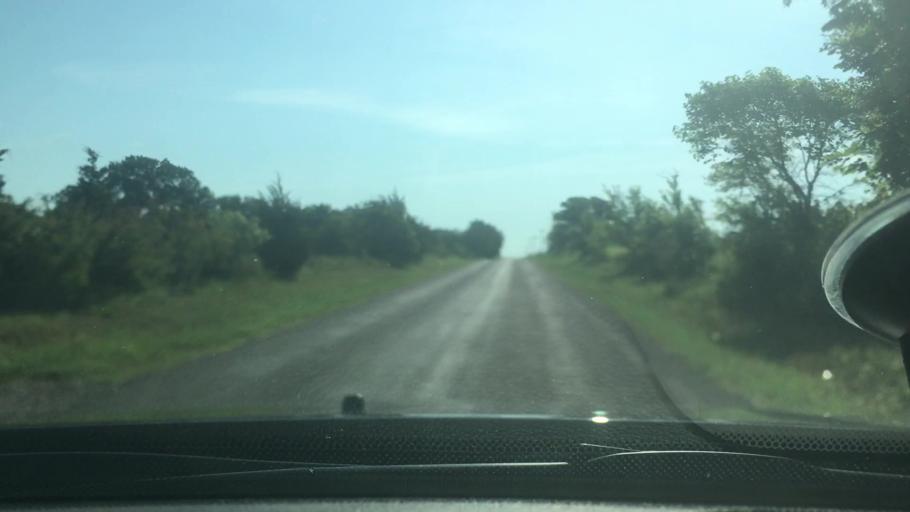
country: US
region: Oklahoma
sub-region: Garvin County
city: Maysville
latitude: 34.6520
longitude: -97.3898
